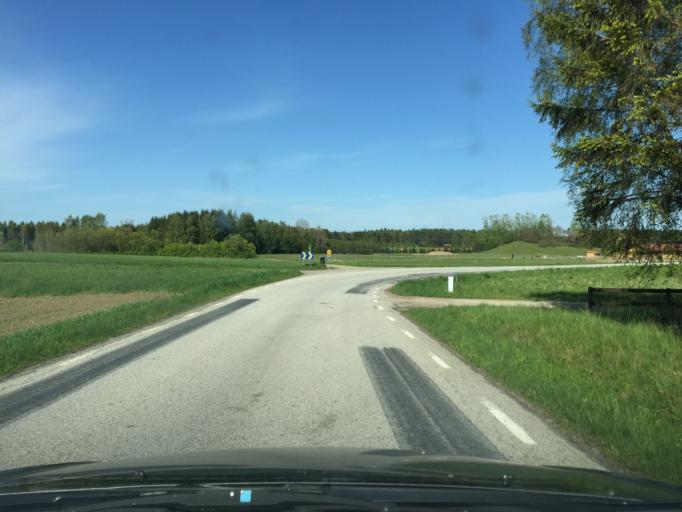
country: SE
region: Skane
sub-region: Sjobo Kommun
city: Blentarp
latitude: 55.5731
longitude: 13.5755
